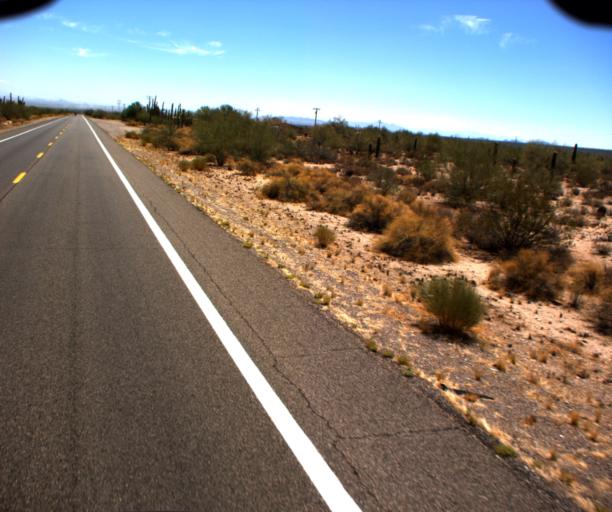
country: US
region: Arizona
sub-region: Pinal County
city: Maricopa
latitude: 32.8379
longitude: -112.1240
